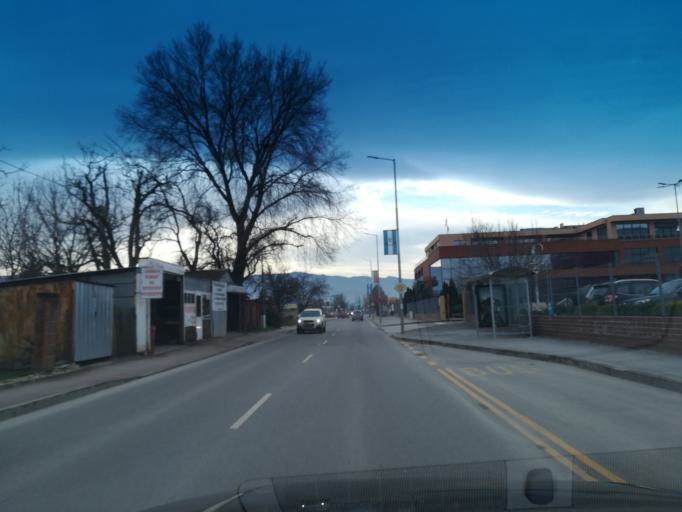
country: BG
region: Plovdiv
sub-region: Obshtina Plovdiv
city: Plovdiv
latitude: 42.1219
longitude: 24.7170
